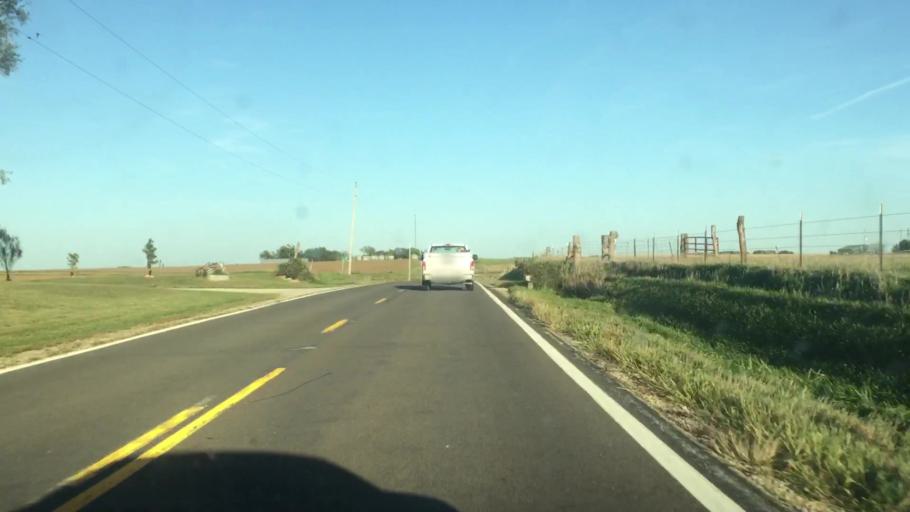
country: US
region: Kansas
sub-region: Brown County
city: Horton
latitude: 39.5515
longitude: -95.4435
